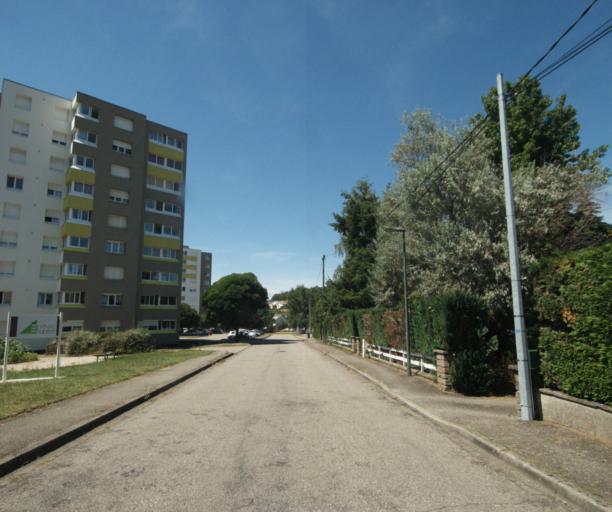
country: FR
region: Lorraine
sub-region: Departement des Vosges
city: Epinal
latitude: 48.1942
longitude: 6.4605
